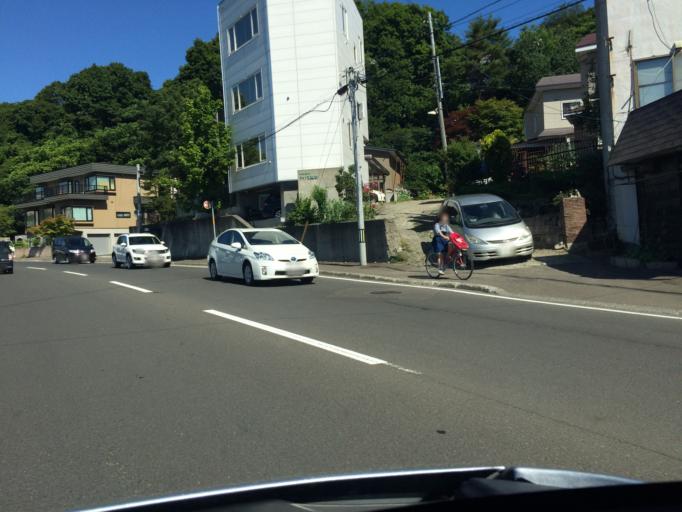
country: JP
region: Hokkaido
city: Sapporo
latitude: 43.0004
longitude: 141.3336
